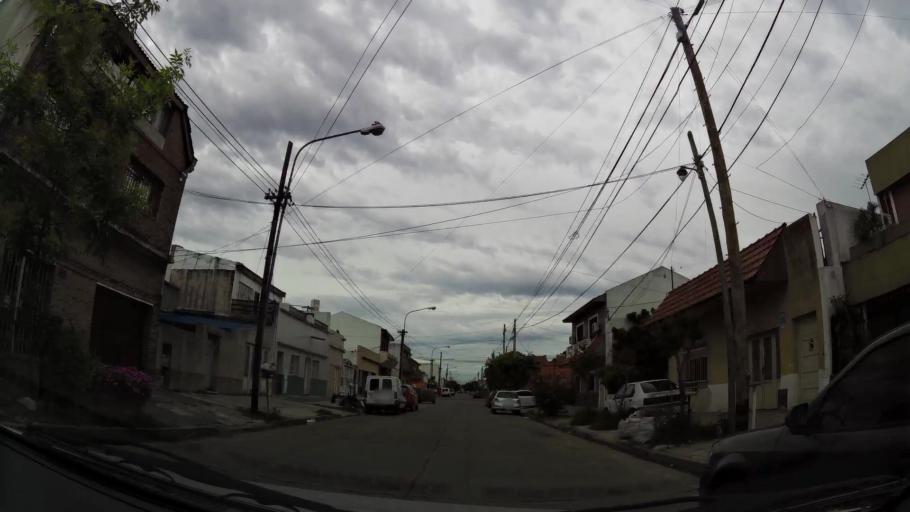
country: AR
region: Buenos Aires
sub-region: Partido de Lanus
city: Lanus
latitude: -34.6814
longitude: -58.3989
